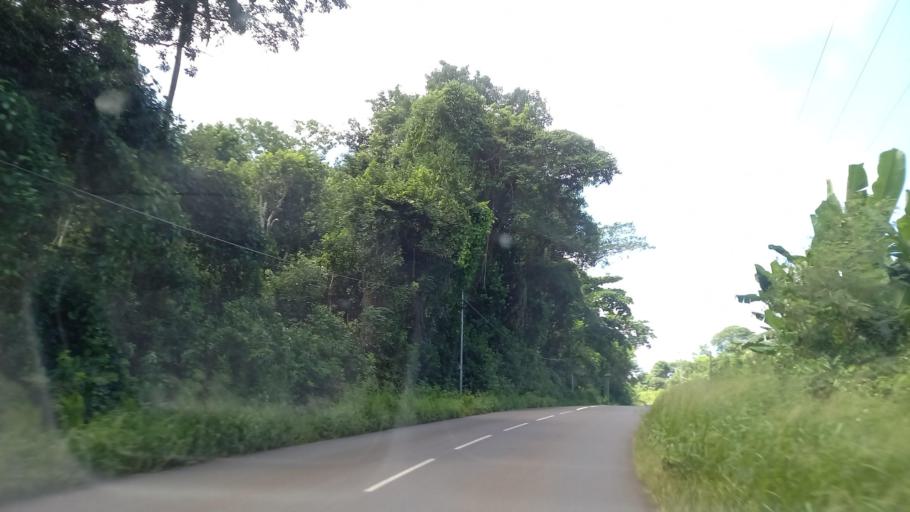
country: YT
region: Acoua
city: Acoua
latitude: -12.7461
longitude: 45.0567
